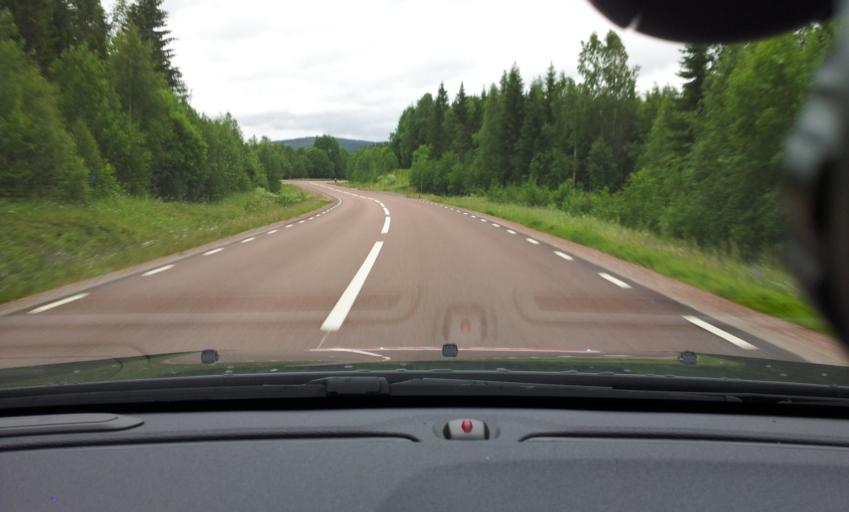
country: SE
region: Jaemtland
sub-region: Ragunda Kommun
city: Hammarstrand
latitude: 63.0294
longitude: 16.5241
